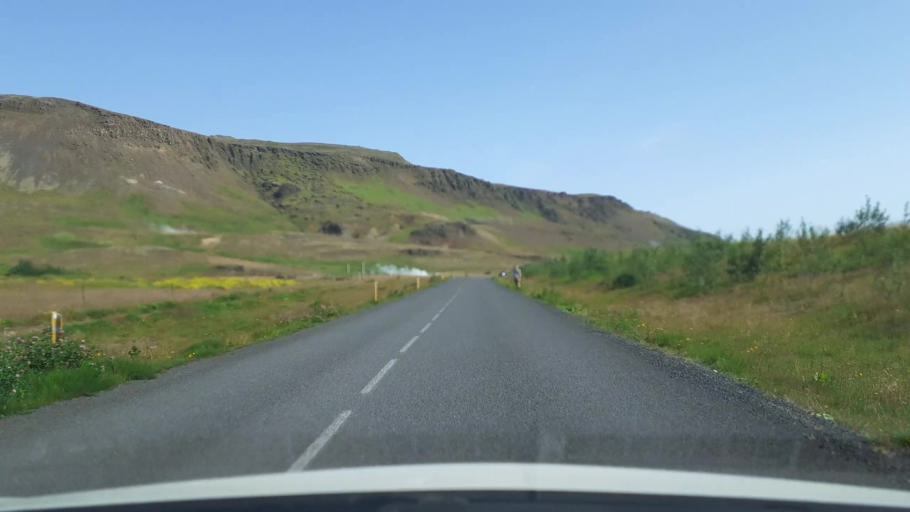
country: IS
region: South
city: Hveragerdi
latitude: 64.0130
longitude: -21.1961
